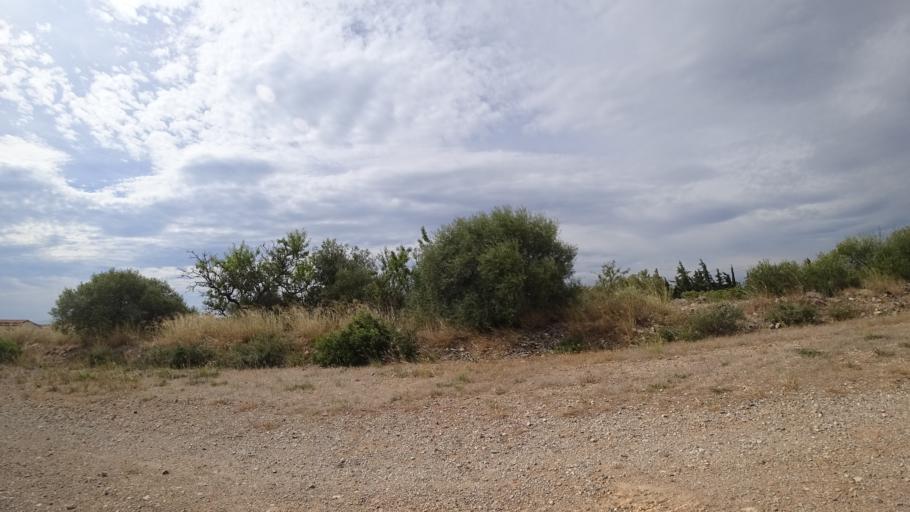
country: FR
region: Languedoc-Roussillon
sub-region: Departement de l'Aude
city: Leucate
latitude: 42.9066
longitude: 3.0279
